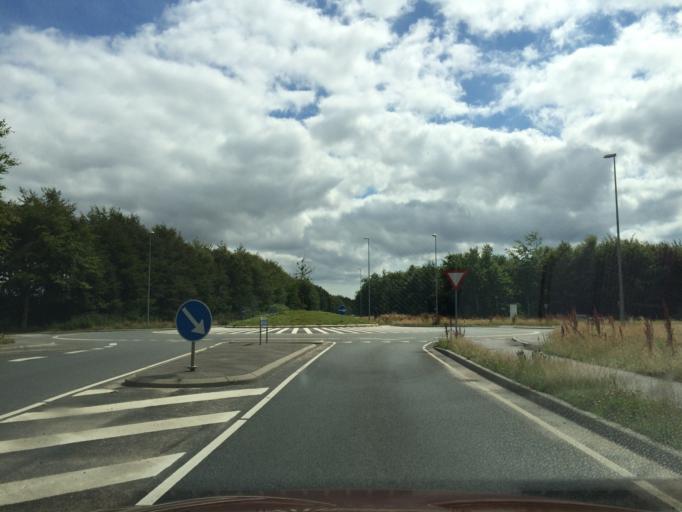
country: DK
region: Central Jutland
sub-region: Silkeborg Kommune
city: Silkeborg
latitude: 56.1954
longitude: 9.6015
